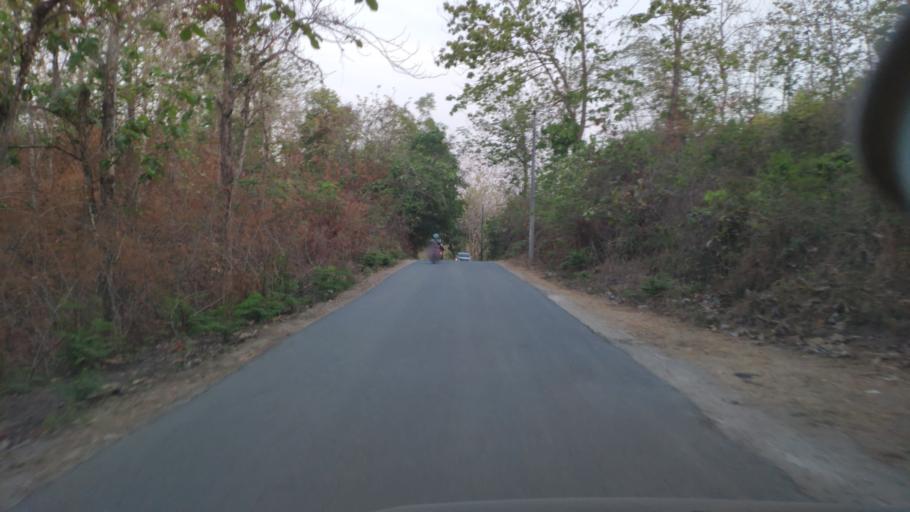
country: ID
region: Central Java
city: Semanggi
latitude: -7.0753
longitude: 111.4164
